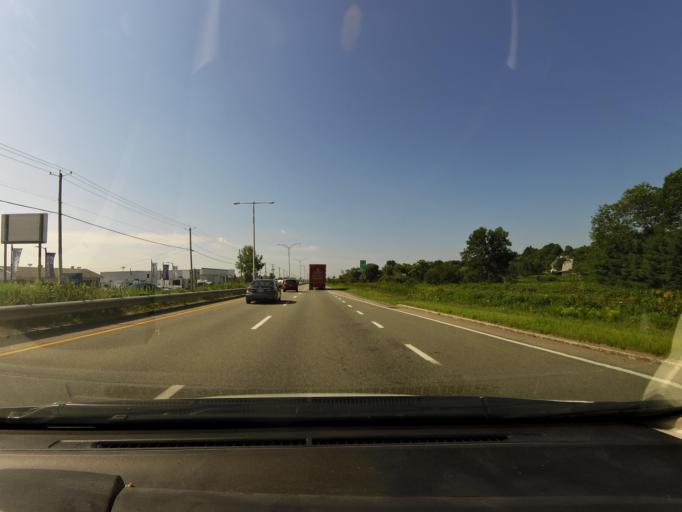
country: CA
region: Quebec
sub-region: Capitale-Nationale
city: Chateau-Richer
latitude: 46.9362
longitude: -71.0577
